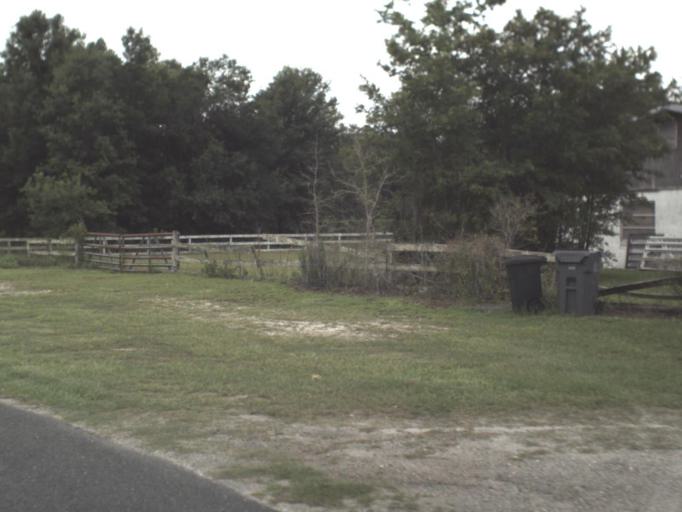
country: US
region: Florida
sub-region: Levy County
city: Williston
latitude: 29.2952
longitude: -82.4476
